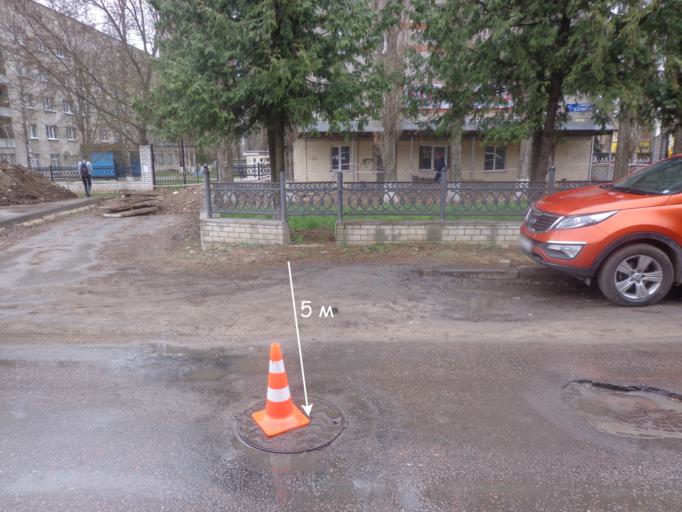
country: RU
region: Voronezj
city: Voronezh
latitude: 51.7154
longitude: 39.2287
